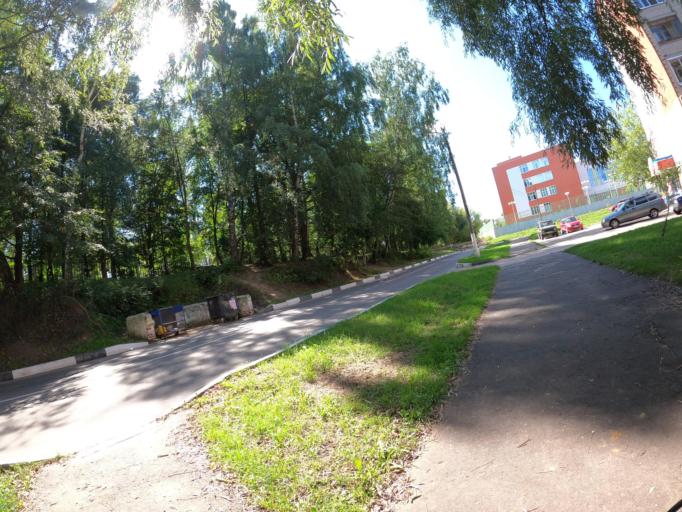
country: RU
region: Moskovskaya
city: Stupino
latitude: 54.8838
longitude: 38.0874
